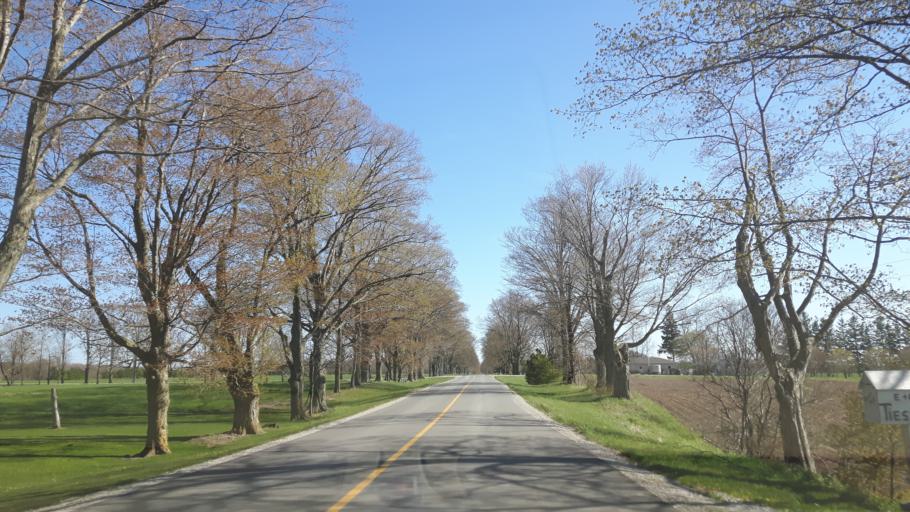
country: CA
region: Ontario
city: Goderich
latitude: 43.6256
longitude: -81.6644
